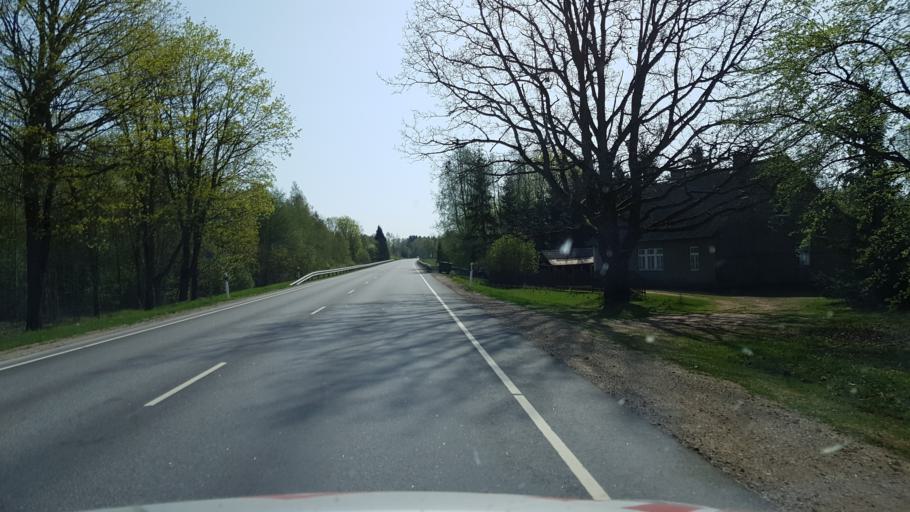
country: EE
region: Paernumaa
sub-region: Saarde vald
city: Kilingi-Nomme
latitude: 58.1580
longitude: 24.8823
